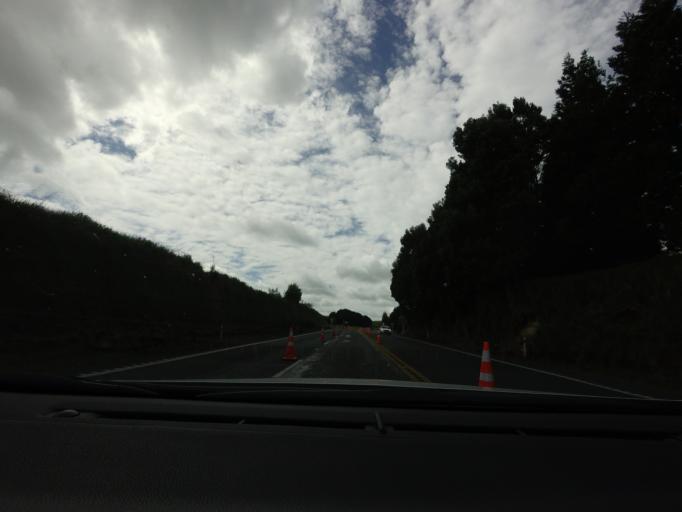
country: NZ
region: Bay of Plenty
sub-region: Rotorua District
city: Rotorua
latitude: -38.2475
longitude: 176.3149
